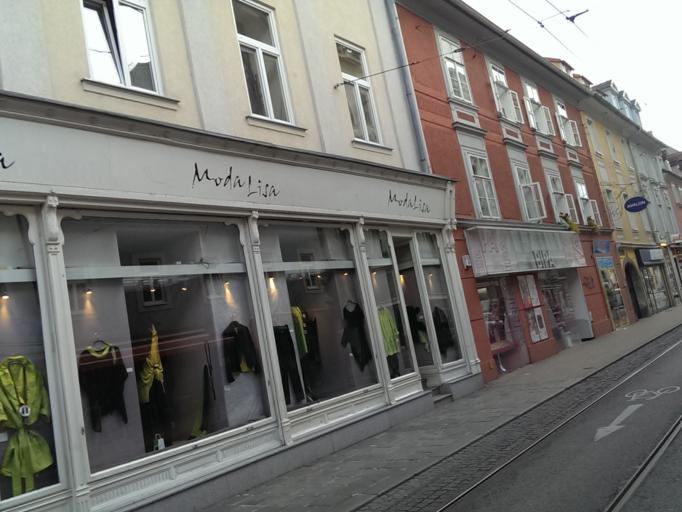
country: AT
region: Styria
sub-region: Graz Stadt
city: Graz
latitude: 47.0670
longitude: 15.4445
